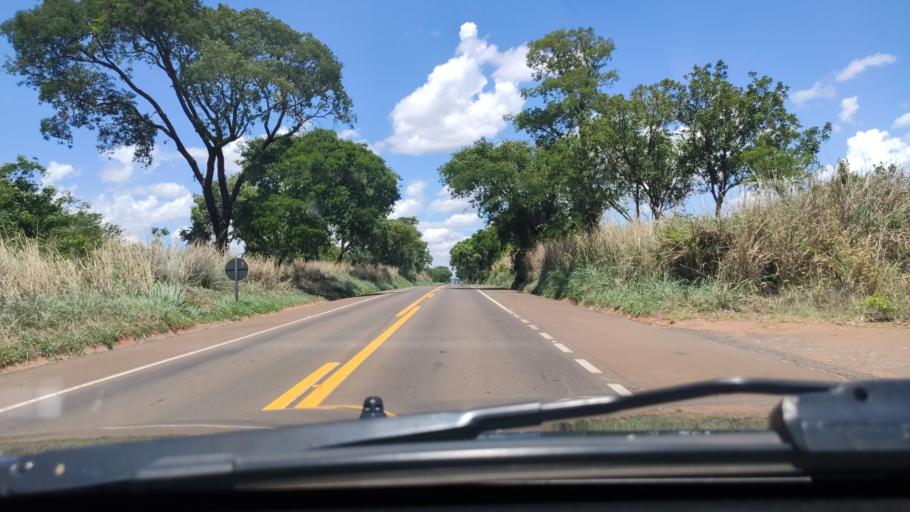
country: BR
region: Sao Paulo
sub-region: Boa Esperanca Do Sul
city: Boa Esperanca do Sul
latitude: -22.0694
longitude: -48.3956
